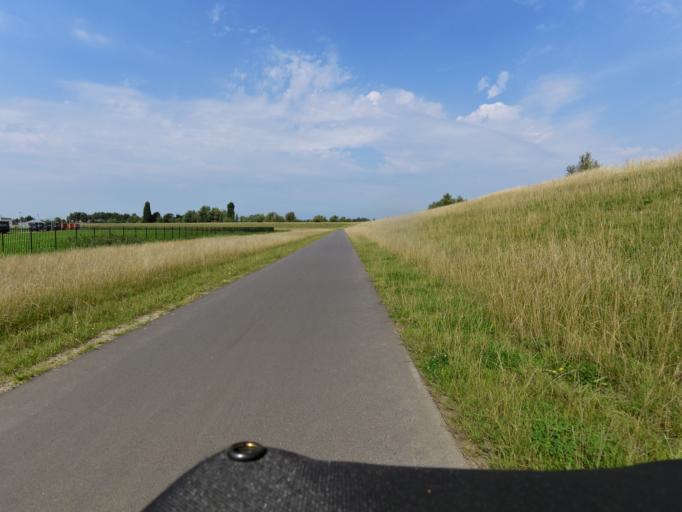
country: NL
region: South Holland
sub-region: Gemeente Oud-Beijerland
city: Oud-Beijerland
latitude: 51.8302
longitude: 4.4441
